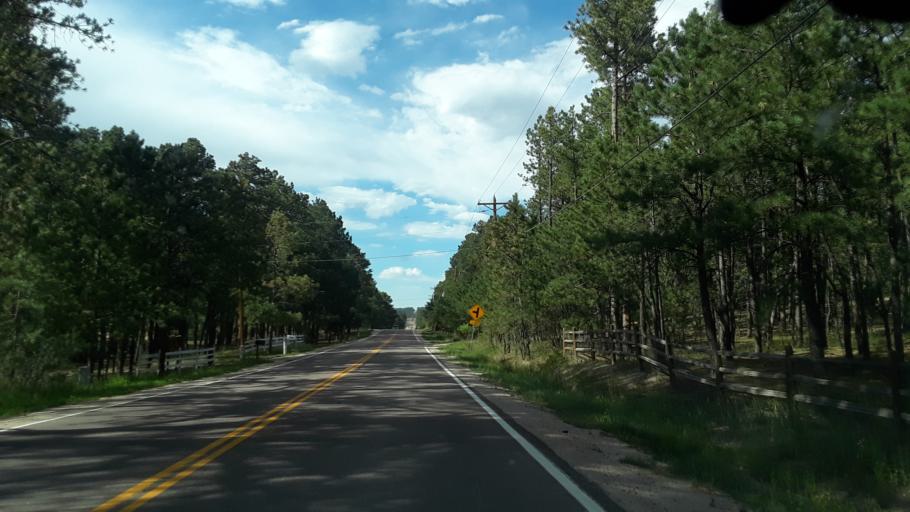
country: US
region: Colorado
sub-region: El Paso County
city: Black Forest
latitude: 39.0007
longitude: -104.7004
